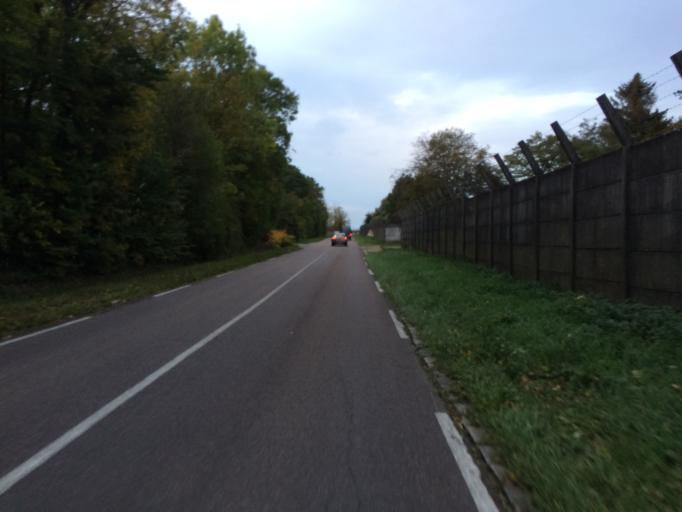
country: FR
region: Ile-de-France
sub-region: Departement des Yvelines
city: Velizy-Villacoublay
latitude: 48.7692
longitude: 2.1915
